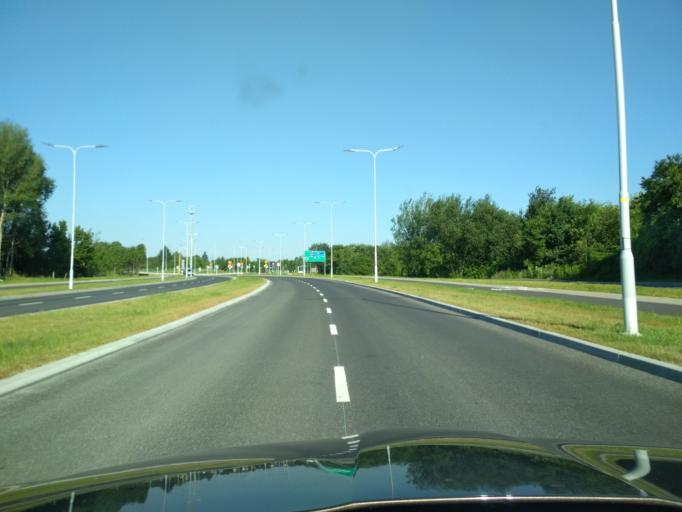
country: PL
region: Subcarpathian Voivodeship
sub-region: Rzeszow
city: Rzeszow
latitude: 50.0654
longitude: 21.9978
